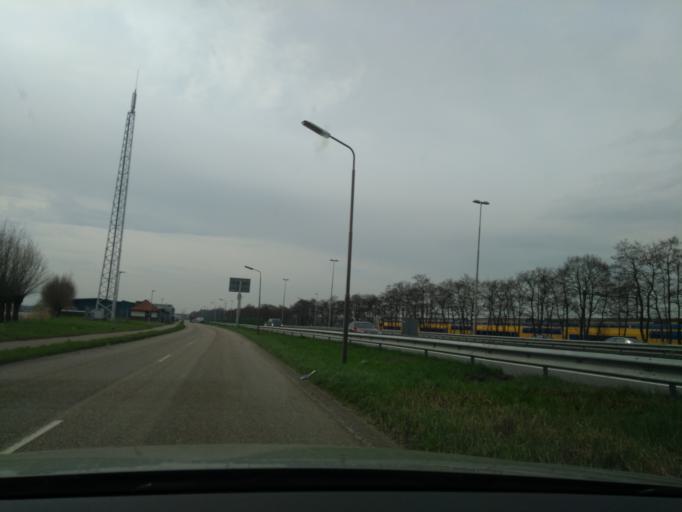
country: NL
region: North Holland
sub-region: Gemeente Haarlem
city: Haarlem
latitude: 52.3865
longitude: 4.7295
